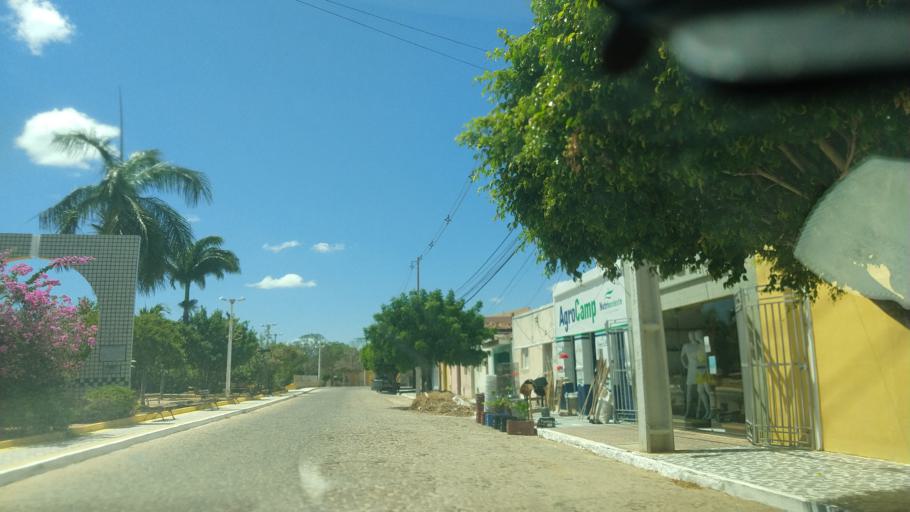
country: BR
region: Rio Grande do Norte
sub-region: Cerro Cora
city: Cerro Cora
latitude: -6.0473
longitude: -36.3477
